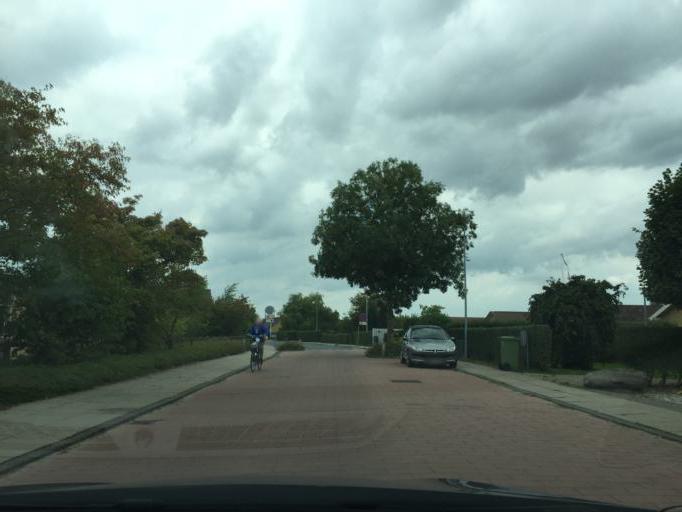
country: DK
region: South Denmark
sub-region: Odense Kommune
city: Stige
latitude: 55.4375
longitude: 10.4070
